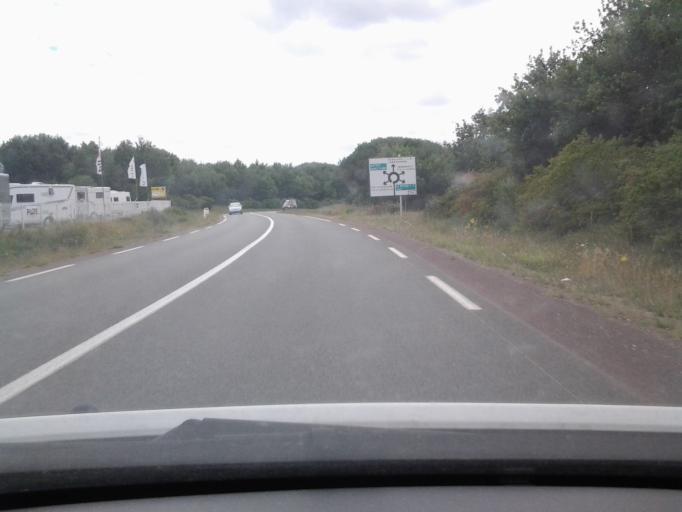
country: FR
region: Pays de la Loire
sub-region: Departement de la Vendee
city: Les Clouzeaux
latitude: 46.6501
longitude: -1.5087
